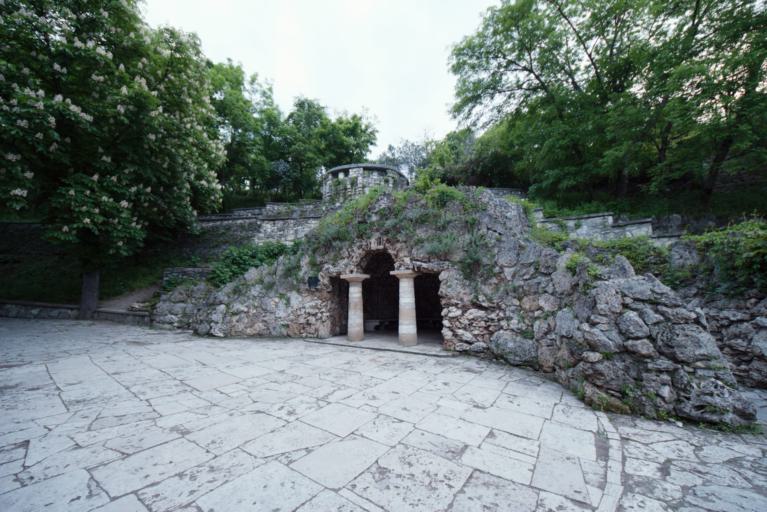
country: RU
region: Stavropol'skiy
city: Goryachevodskiy
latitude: 44.0359
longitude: 43.0817
